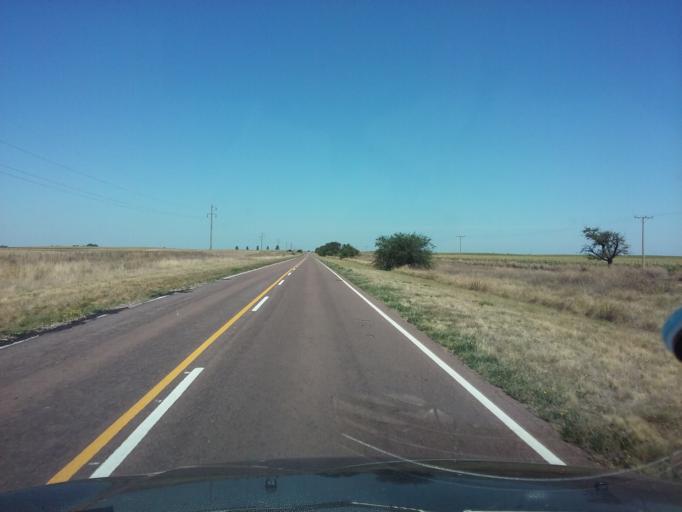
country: AR
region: La Pampa
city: Anguil
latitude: -36.4835
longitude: -63.9436
